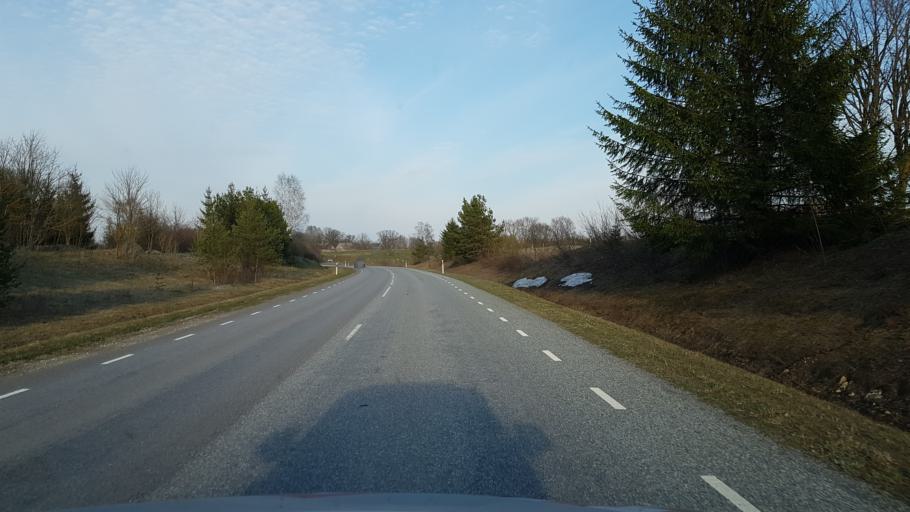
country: EE
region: Laeaene-Virumaa
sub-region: Vinni vald
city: Vinni
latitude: 59.3177
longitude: 26.4792
